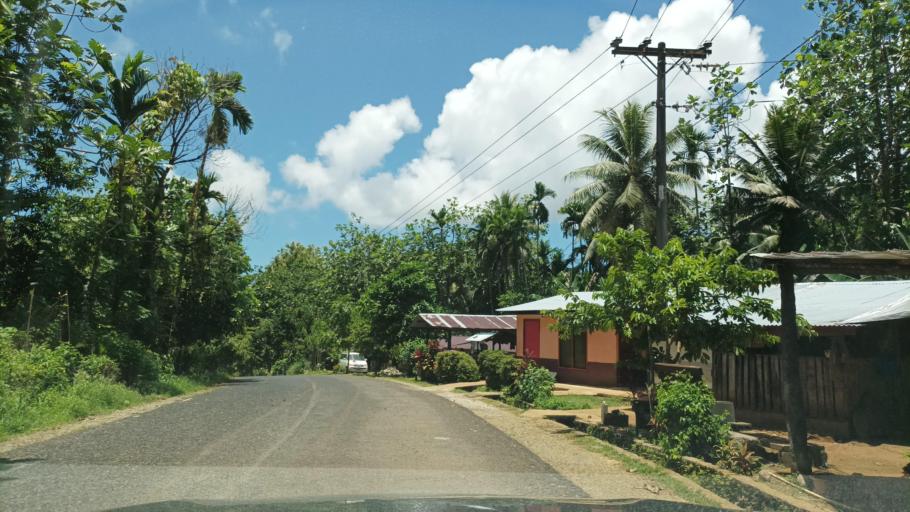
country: FM
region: Pohnpei
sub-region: Madolenihm Municipality
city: Madolenihm Municipality Government
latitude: 6.8716
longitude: 158.2857
